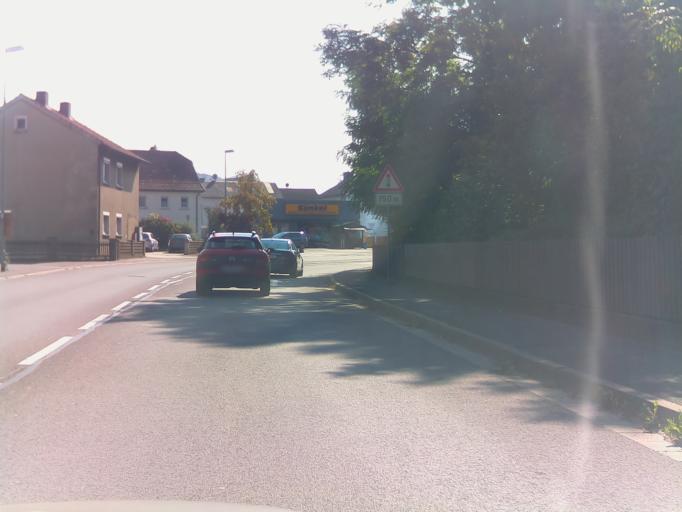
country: DE
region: Bavaria
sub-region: Upper Franconia
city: Hochstadt am Main
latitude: 50.1514
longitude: 11.1729
